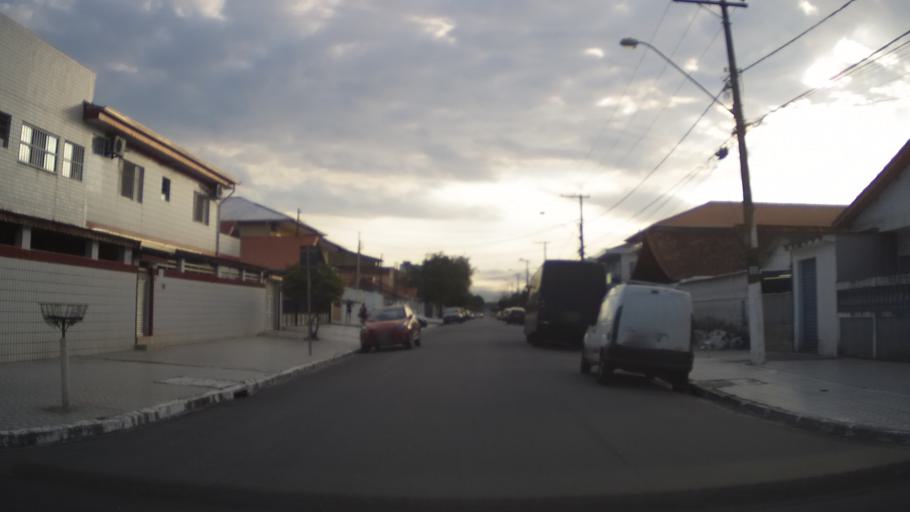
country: BR
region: Sao Paulo
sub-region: Praia Grande
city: Praia Grande
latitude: -23.9973
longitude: -46.4177
